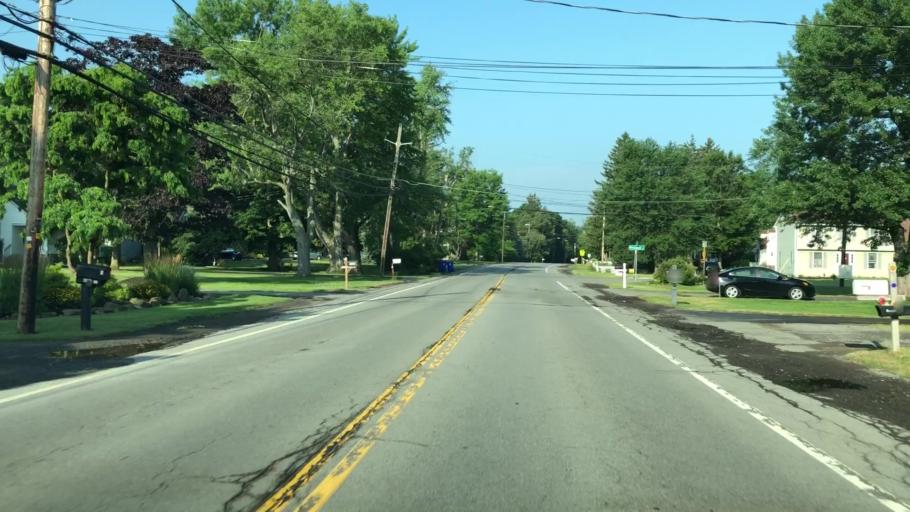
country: US
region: New York
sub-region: Erie County
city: Orchard Park
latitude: 42.8319
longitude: -78.7239
